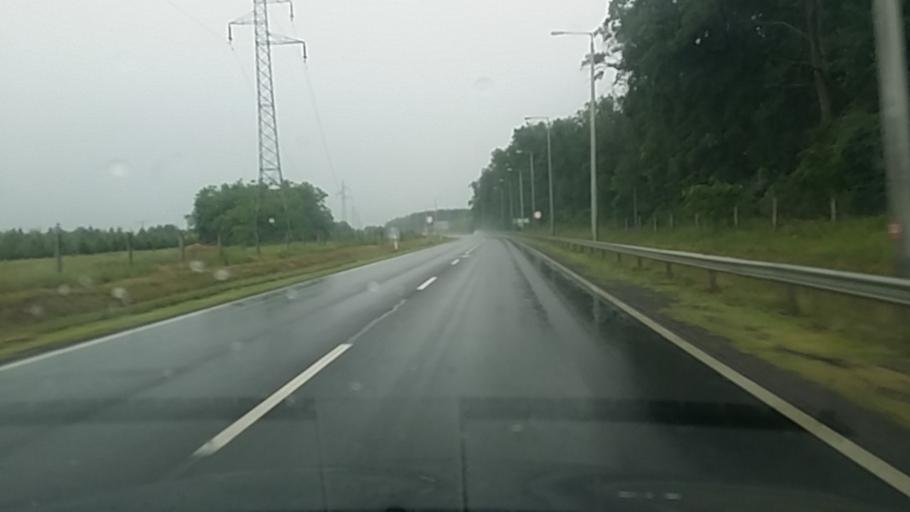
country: HU
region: Hajdu-Bihar
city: Hajduhadhaz
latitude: 47.6533
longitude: 21.6507
